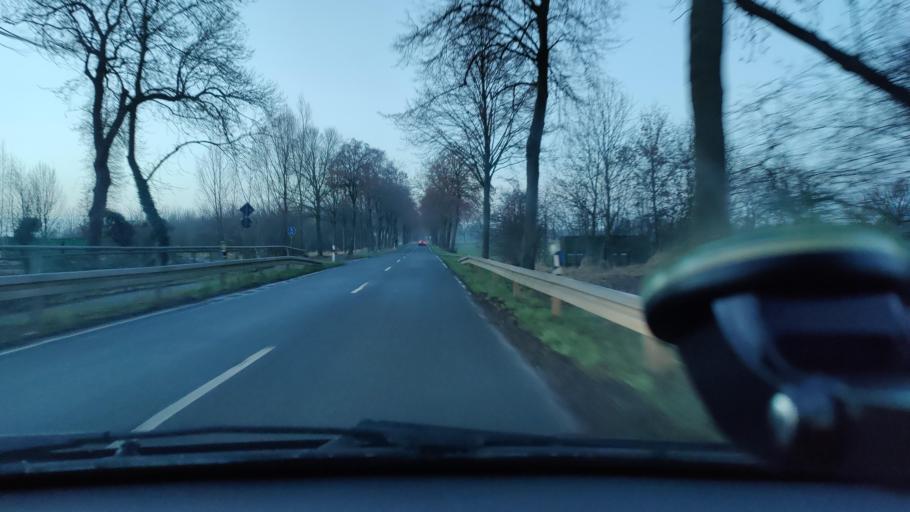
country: DE
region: North Rhine-Westphalia
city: Rheinberg
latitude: 51.5794
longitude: 6.6180
